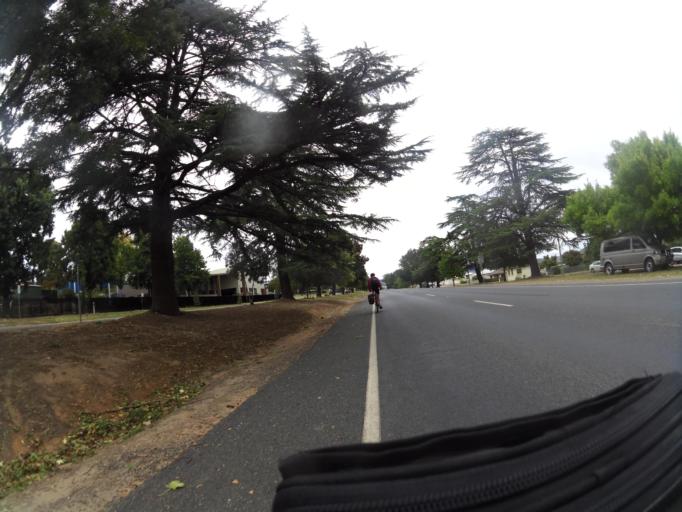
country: AU
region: New South Wales
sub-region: Snowy River
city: Jindabyne
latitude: -36.1918
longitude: 147.9110
